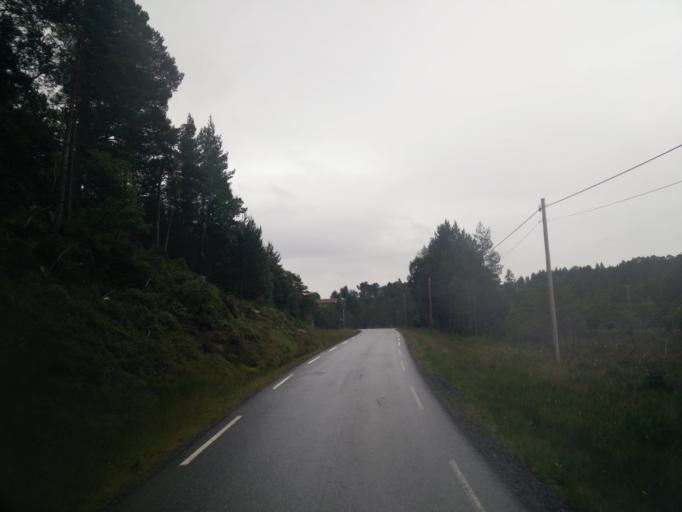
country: NO
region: More og Romsdal
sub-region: Kristiansund
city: Rensvik
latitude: 63.0398
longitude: 7.9420
